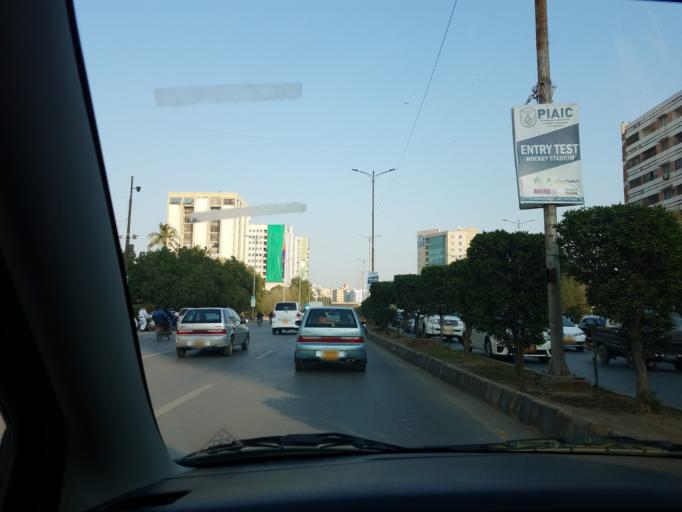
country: PK
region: Sindh
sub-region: Karachi District
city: Karachi
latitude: 24.8598
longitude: 67.0545
